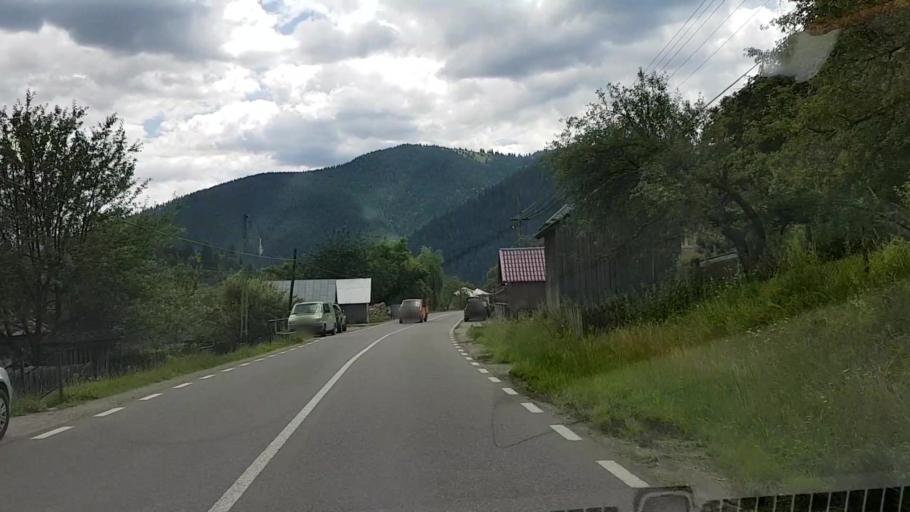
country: RO
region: Neamt
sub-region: Comuna Borca
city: Borca
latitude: 47.2125
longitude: 25.7560
